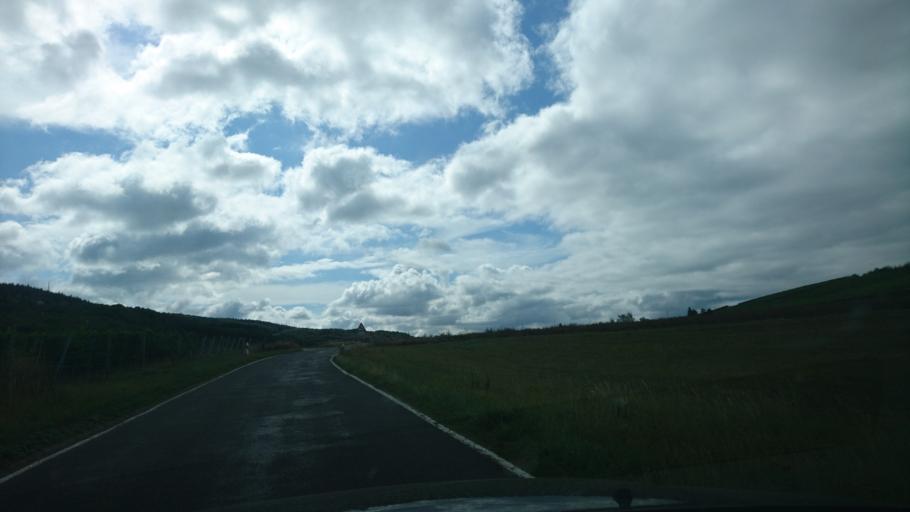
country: DE
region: Rheinland-Pfalz
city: Wiltingen
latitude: 49.6554
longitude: 6.6255
